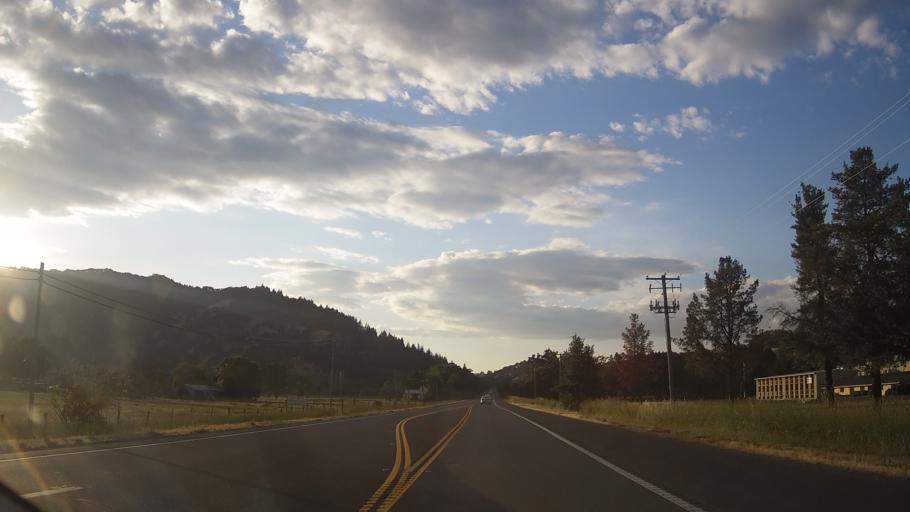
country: US
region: California
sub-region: Mendocino County
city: Talmage
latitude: 39.0448
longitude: -123.1507
